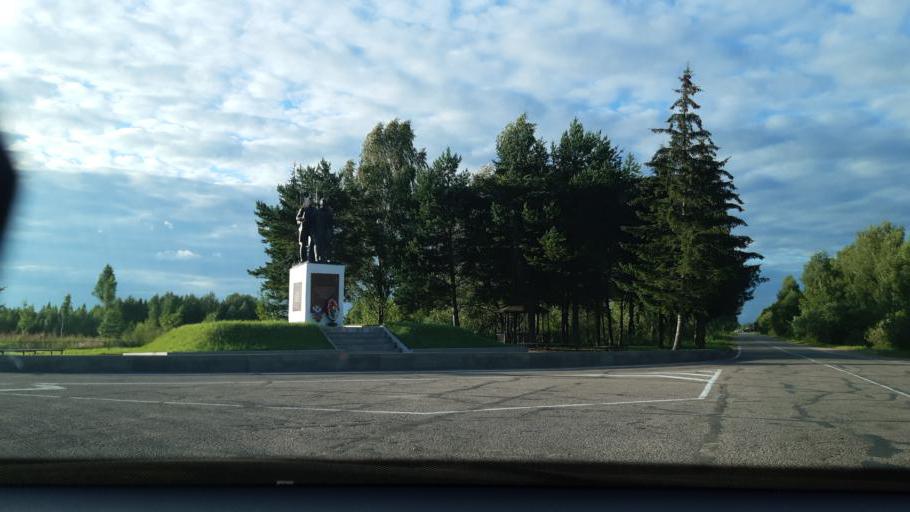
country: RU
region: Smolensk
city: Yel'nya
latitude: 54.5581
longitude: 33.1846
